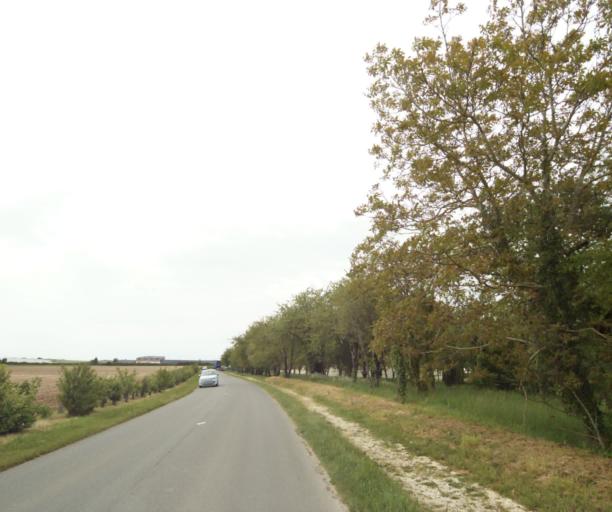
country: FR
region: Poitou-Charentes
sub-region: Departement de la Charente-Maritime
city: Les Gonds
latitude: 45.7085
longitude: -0.6229
